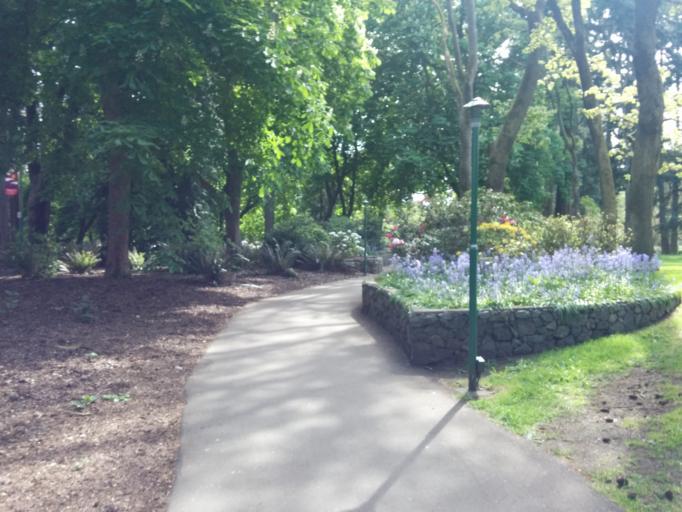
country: CA
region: British Columbia
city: Victoria
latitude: 48.4140
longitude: -123.3639
